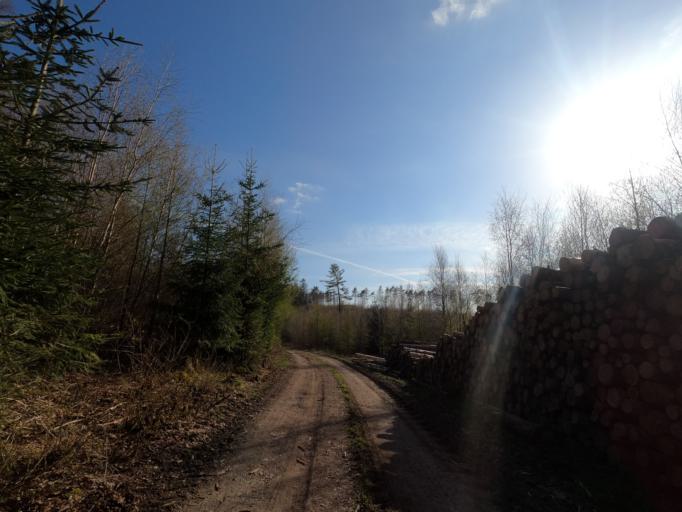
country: DE
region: North Rhine-Westphalia
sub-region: Regierungsbezirk Arnsberg
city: Herscheid
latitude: 51.1770
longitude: 7.7271
